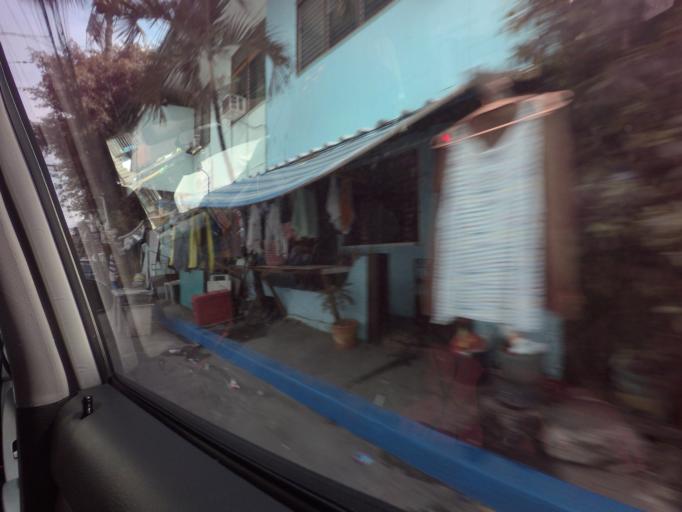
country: PH
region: Metro Manila
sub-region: San Juan
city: San Juan
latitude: 14.6018
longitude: 121.0149
